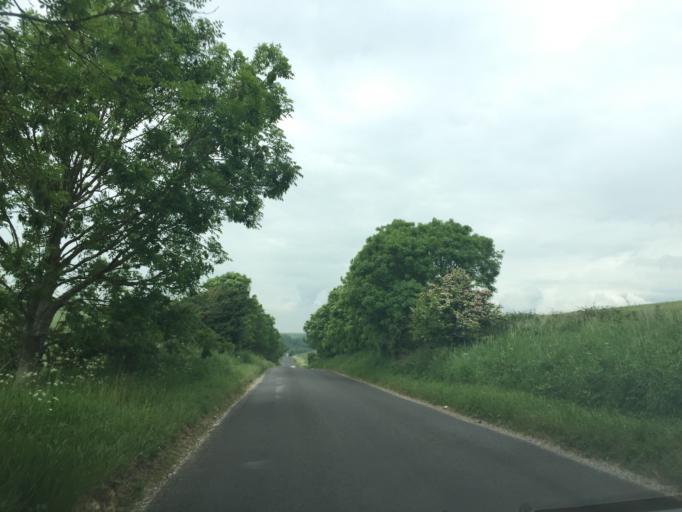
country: GB
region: England
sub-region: Dorset
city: Wool
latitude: 50.6369
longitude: -2.2671
